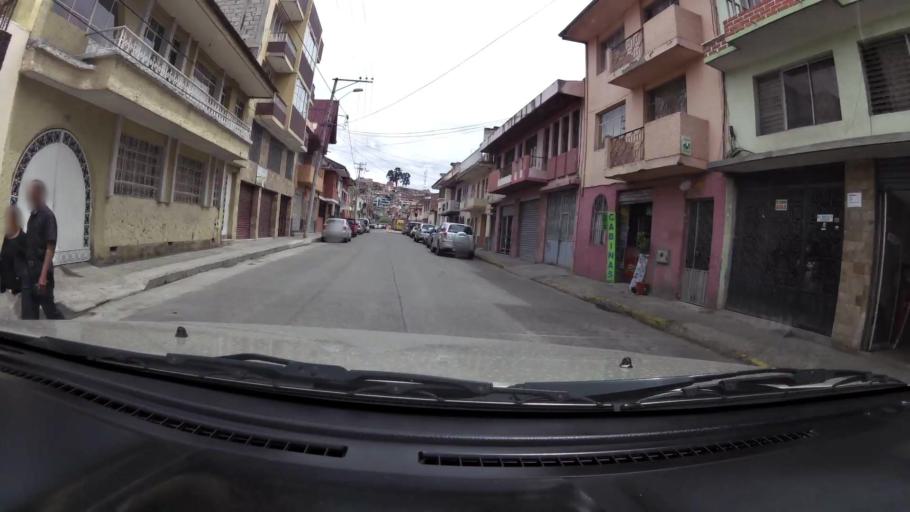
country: EC
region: Azuay
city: Cuenca
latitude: -2.8934
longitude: -79.0136
